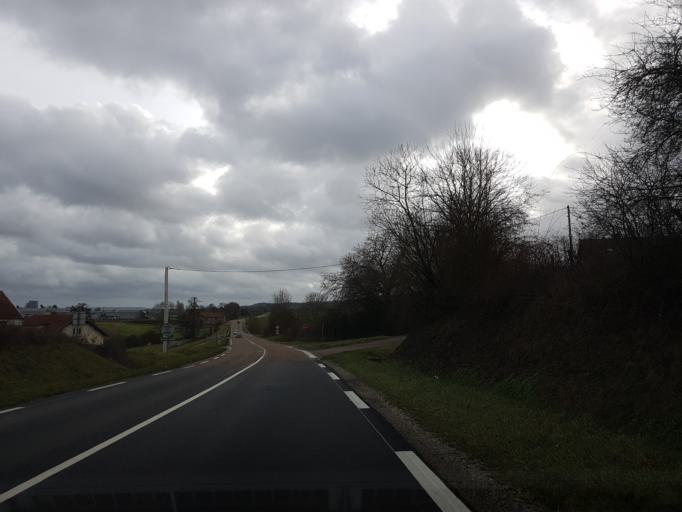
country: FR
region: Champagne-Ardenne
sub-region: Departement de la Haute-Marne
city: Langres
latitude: 47.8632
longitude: 5.3425
